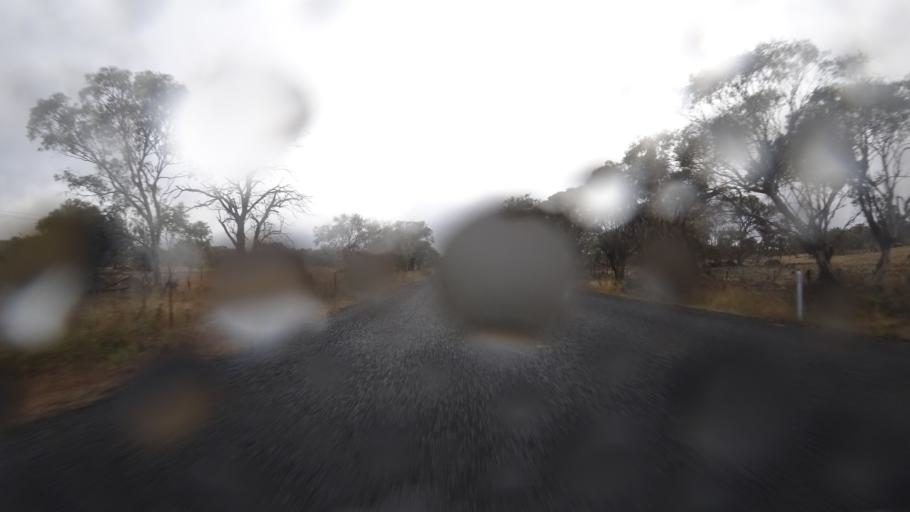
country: AU
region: New South Wales
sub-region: Snowy River
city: Jindabyne
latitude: -36.3619
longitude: 148.7044
